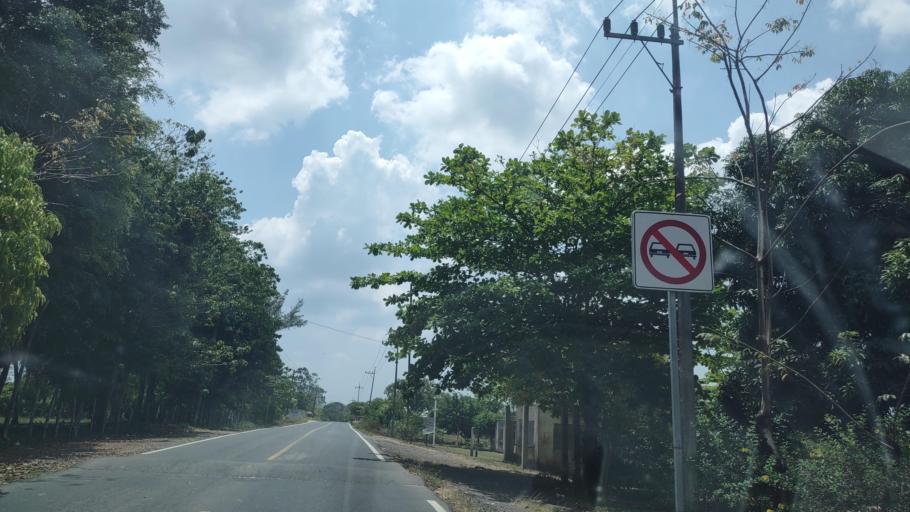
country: MX
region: Veracruz
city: Las Choapas
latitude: 17.9308
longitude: -94.1511
